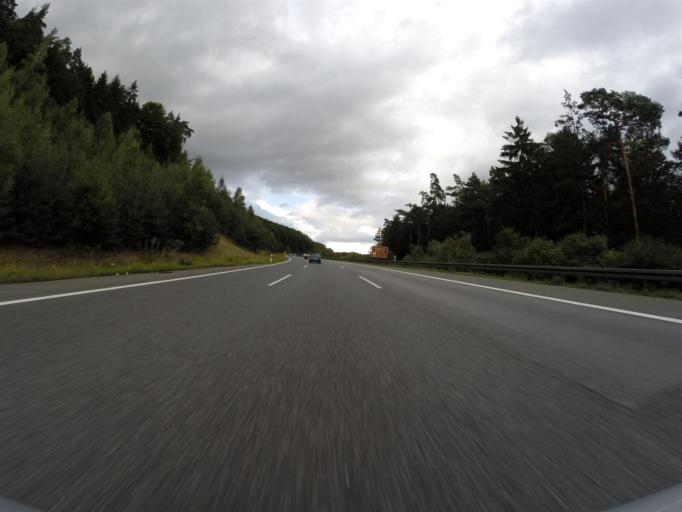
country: DE
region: Bavaria
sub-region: Regierungsbezirk Mittelfranken
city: Simmelsdorf
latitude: 49.5819
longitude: 11.3486
